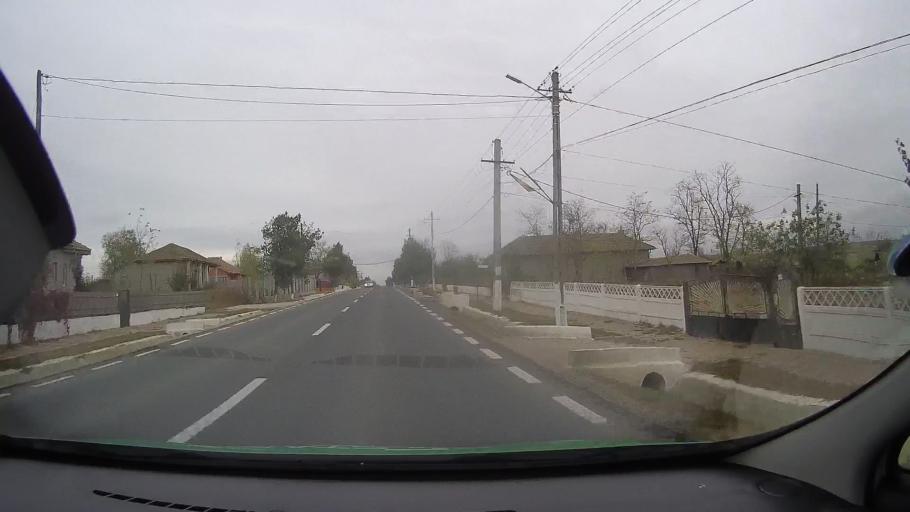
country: RO
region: Constanta
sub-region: Comuna Nicolae Balcescu
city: Dorobantu
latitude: 44.4114
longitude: 28.3230
